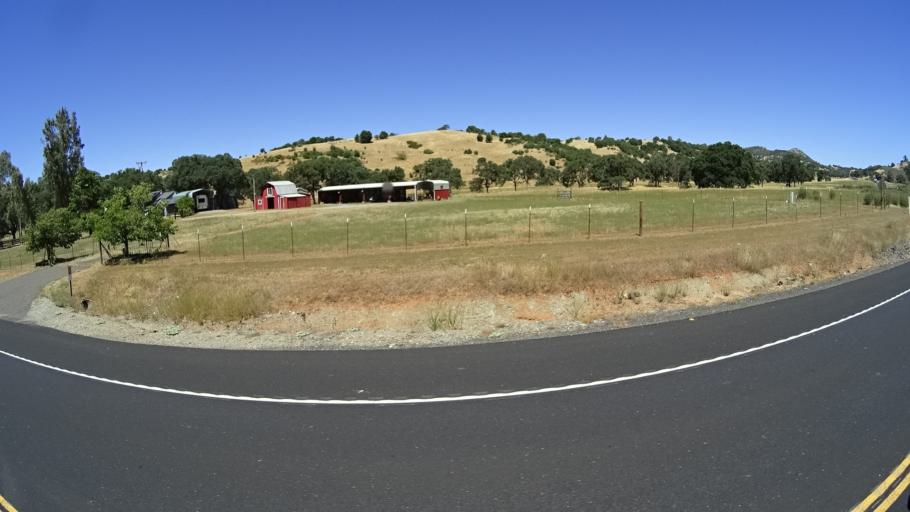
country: US
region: California
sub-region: Calaveras County
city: Copperopolis
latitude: 38.0173
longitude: -120.6425
